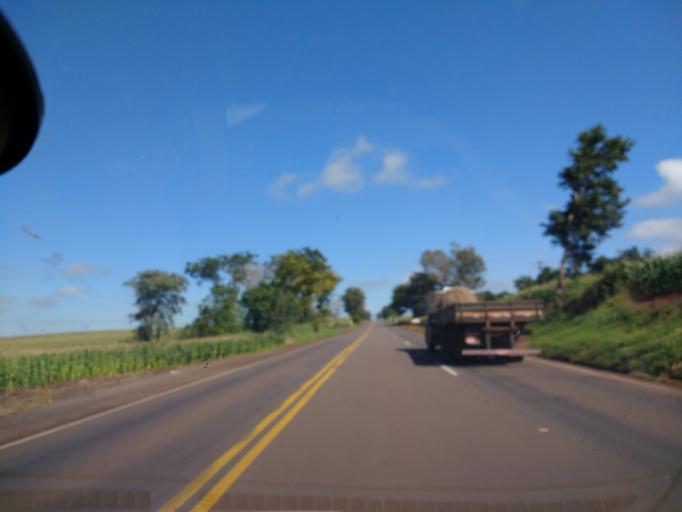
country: BR
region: Parana
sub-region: Terra Boa
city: Terra Boa
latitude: -23.5993
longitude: -52.3962
